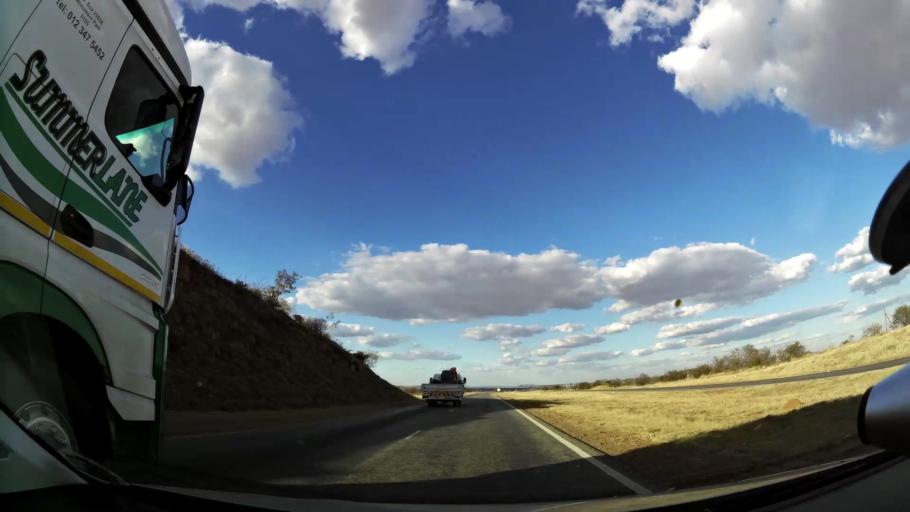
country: ZA
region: North-West
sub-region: Dr Kenneth Kaunda District Municipality
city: Potchefstroom
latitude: -26.7572
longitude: 26.9939
